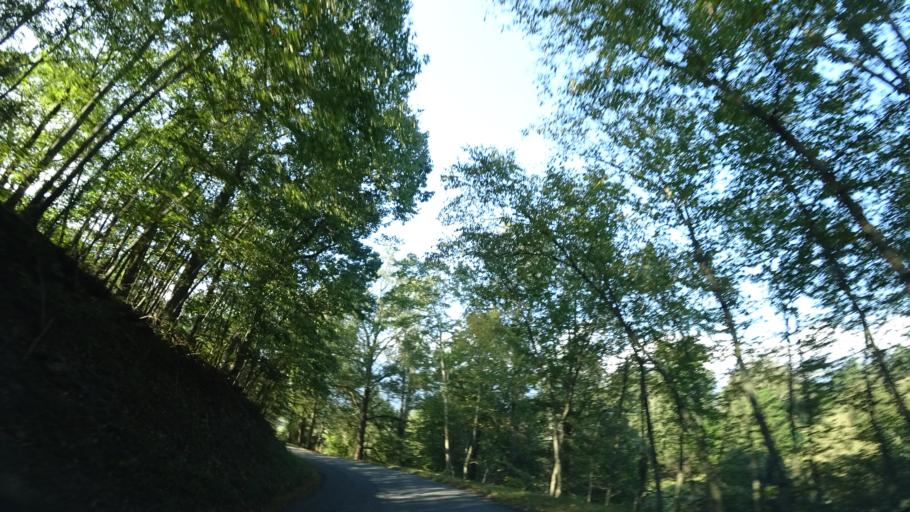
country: US
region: Virginia
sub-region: Madison County
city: Madison
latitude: 38.5036
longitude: -78.3163
